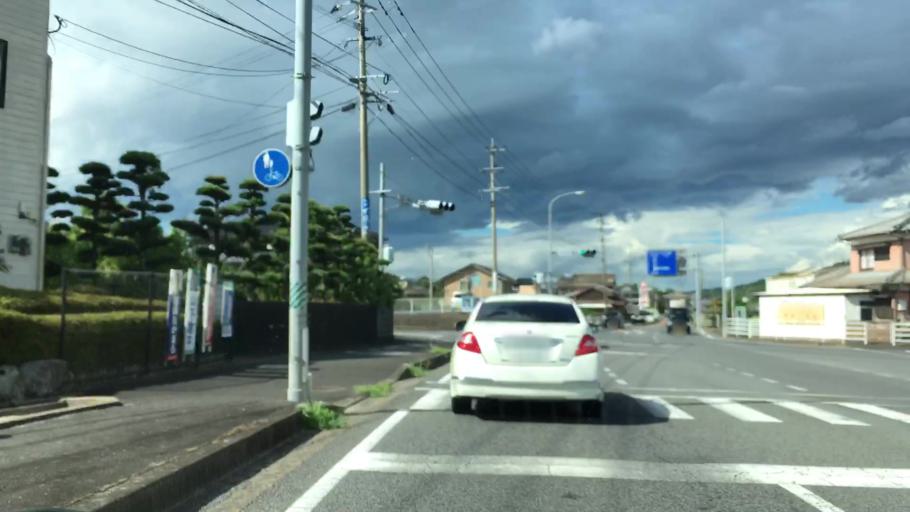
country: JP
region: Saga Prefecture
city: Imaricho-ko
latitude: 33.2253
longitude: 129.8471
